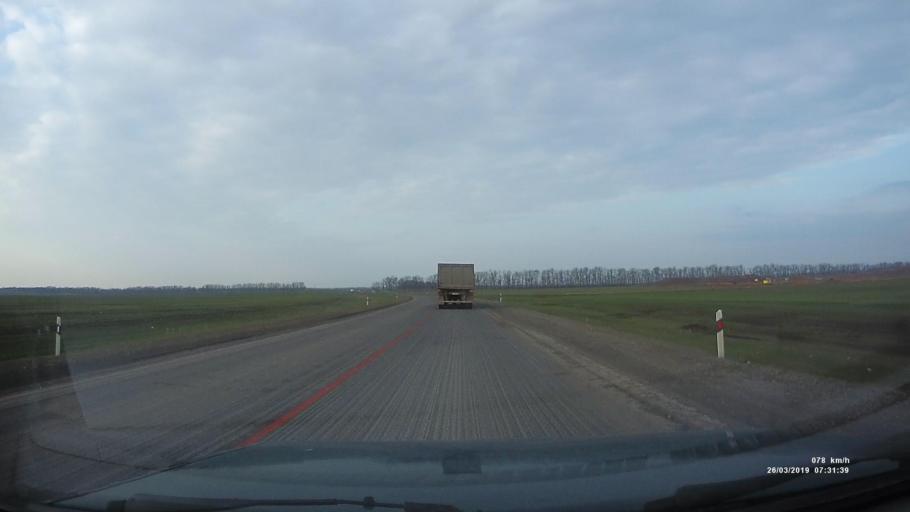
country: RU
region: Rostov
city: Novobessergenovka
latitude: 47.2324
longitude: 38.7876
